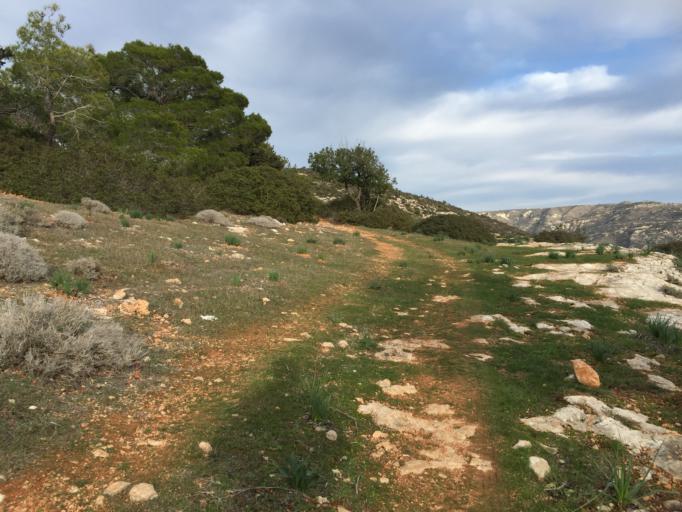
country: CY
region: Pafos
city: Pegeia
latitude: 34.8896
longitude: 32.3755
